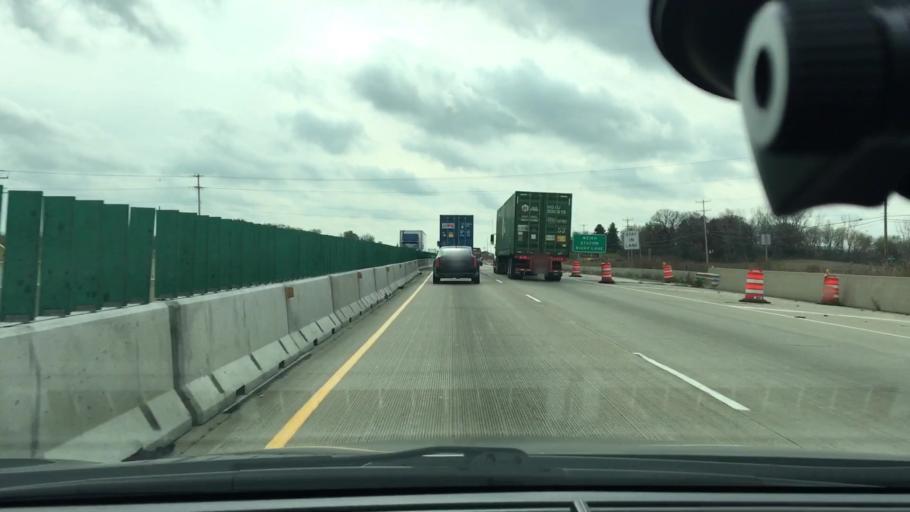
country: US
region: Wisconsin
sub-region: Racine County
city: Caledonia
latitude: 42.8013
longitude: -87.9534
